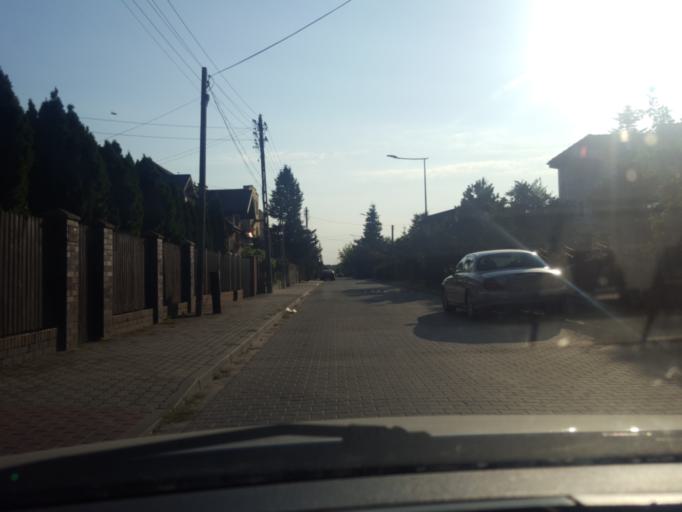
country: PL
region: Masovian Voivodeship
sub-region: Warszawa
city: Rembertow
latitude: 52.2672
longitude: 21.1653
